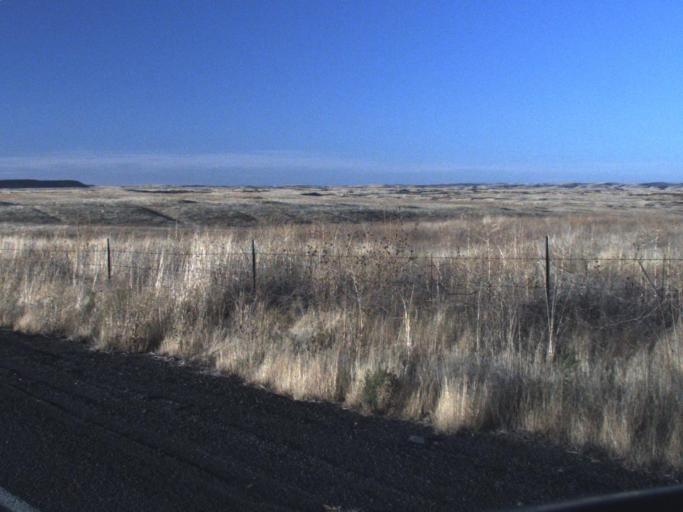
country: US
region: Washington
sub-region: Walla Walla County
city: Waitsburg
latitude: 46.6594
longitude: -118.2690
